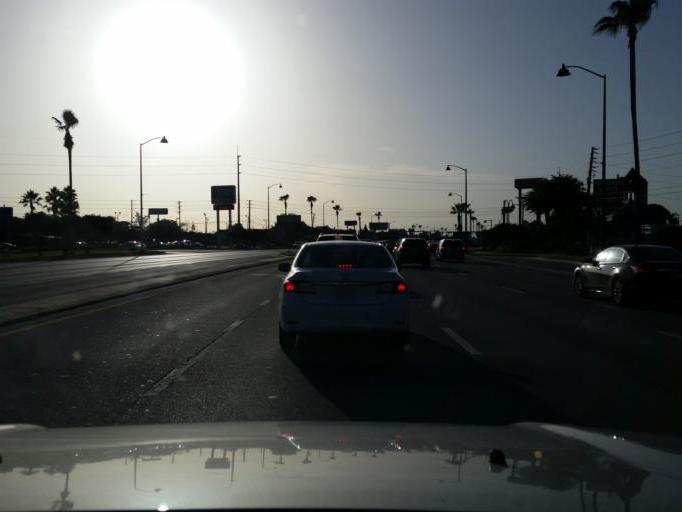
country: US
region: Florida
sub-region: Polk County
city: Citrus Ridge
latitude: 28.3337
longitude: -81.5891
